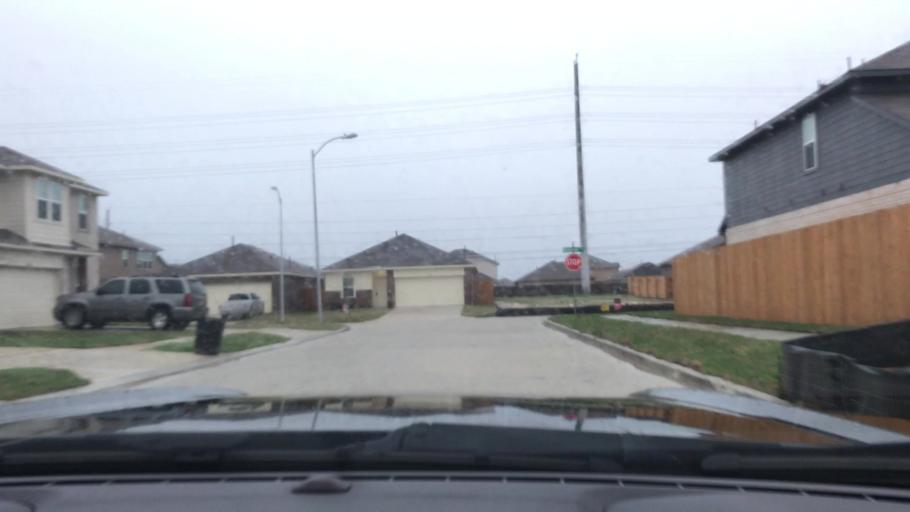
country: US
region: Texas
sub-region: Harris County
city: Humble
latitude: 30.0171
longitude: -95.3109
